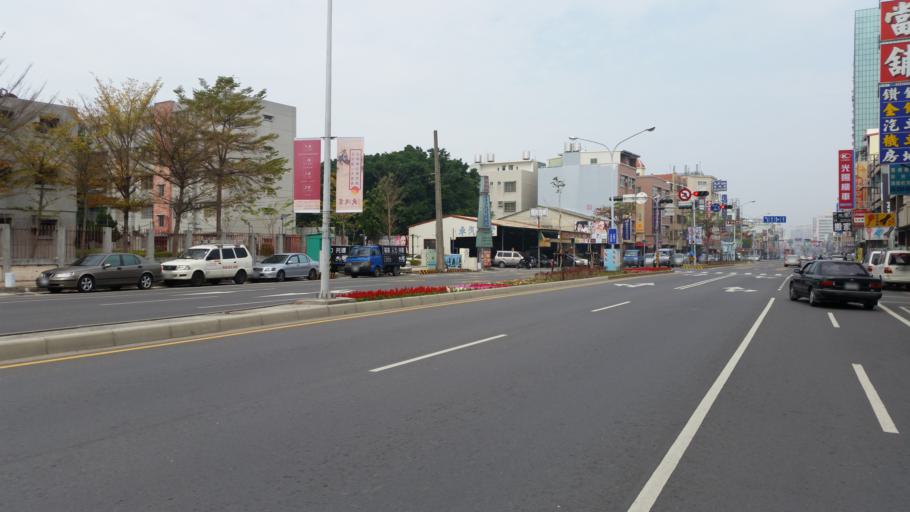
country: TW
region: Taiwan
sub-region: Tainan
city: Tainan
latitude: 22.9653
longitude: 120.2164
